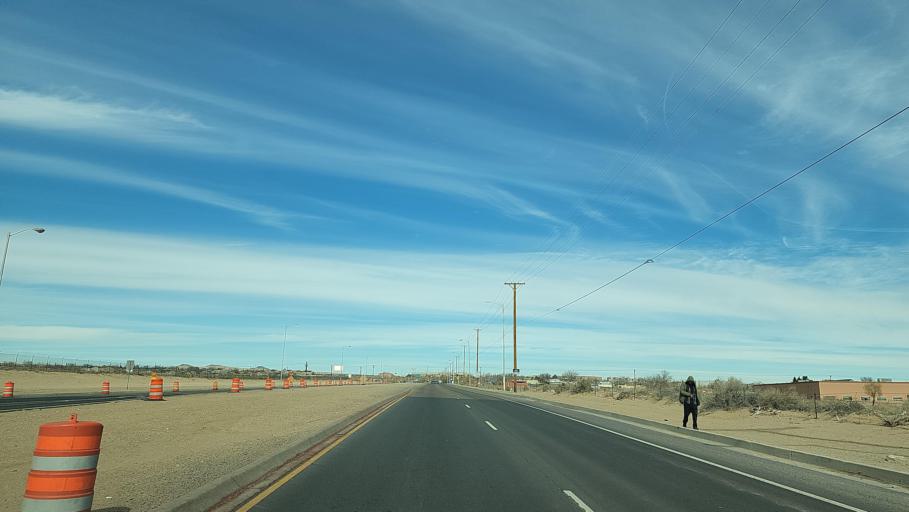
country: US
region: New Mexico
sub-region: Bernalillo County
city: Albuquerque
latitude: 35.0666
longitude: -106.7103
